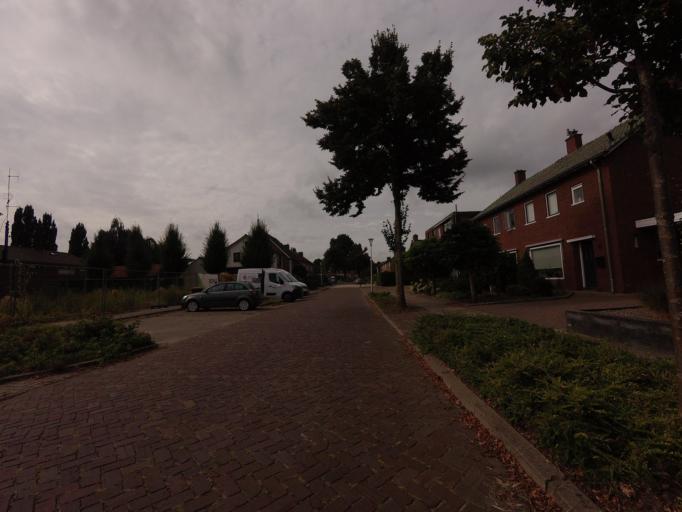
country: DE
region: Lower Saxony
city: Nordhorn
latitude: 52.3781
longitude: 7.0022
